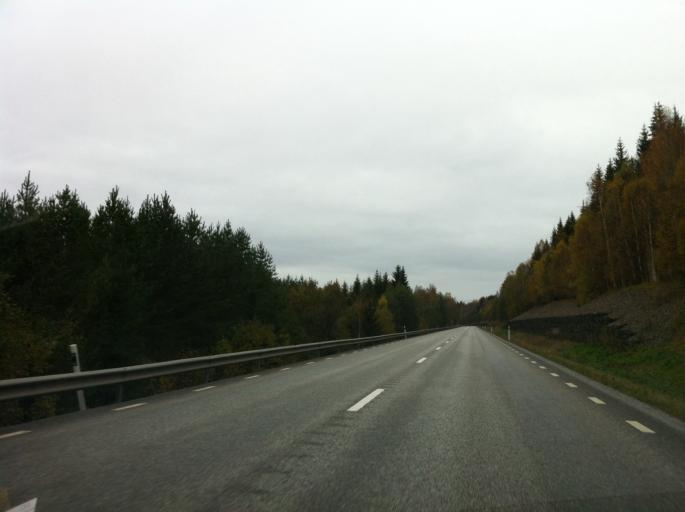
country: SE
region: OErebro
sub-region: Ljusnarsbergs Kommun
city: Kopparberg
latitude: 59.8581
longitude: 15.0600
